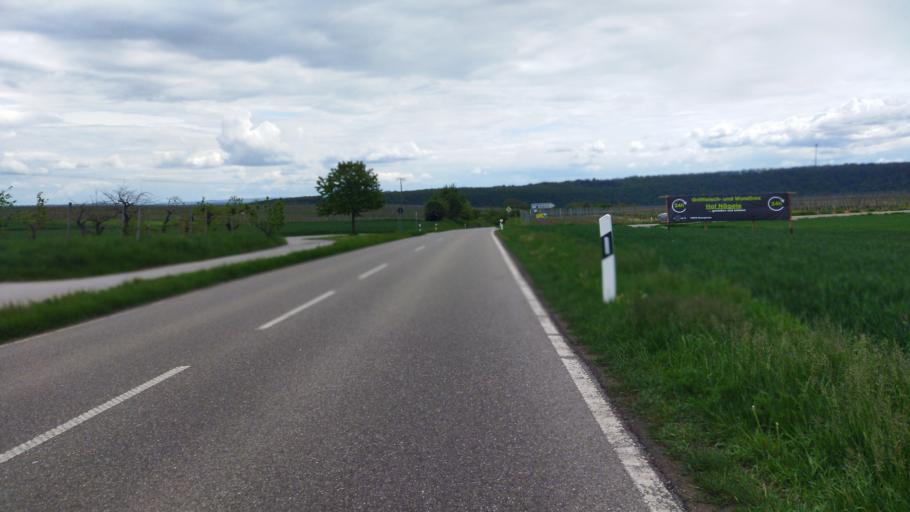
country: DE
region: Baden-Wuerttemberg
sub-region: Regierungsbezirk Stuttgart
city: Hessigheim
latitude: 49.0069
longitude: 9.1877
